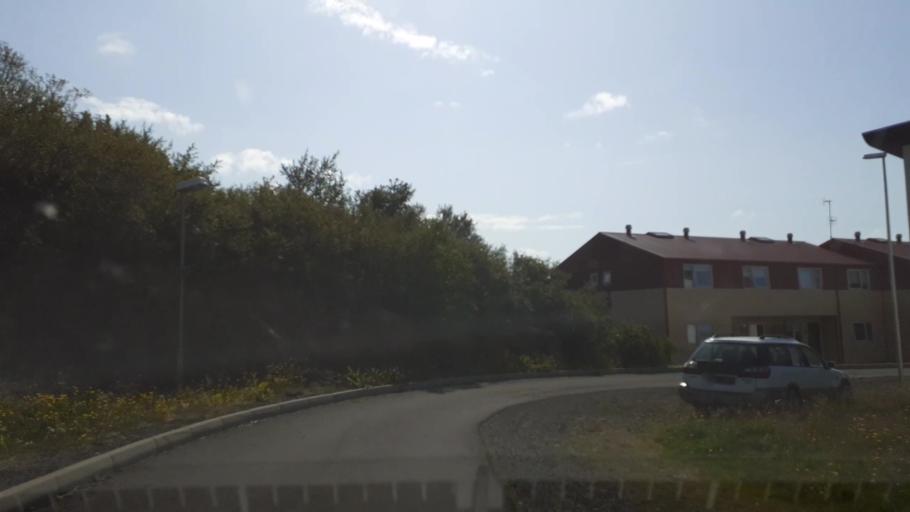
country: IS
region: West
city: Borgarnes
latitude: 64.7680
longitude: -21.5507
